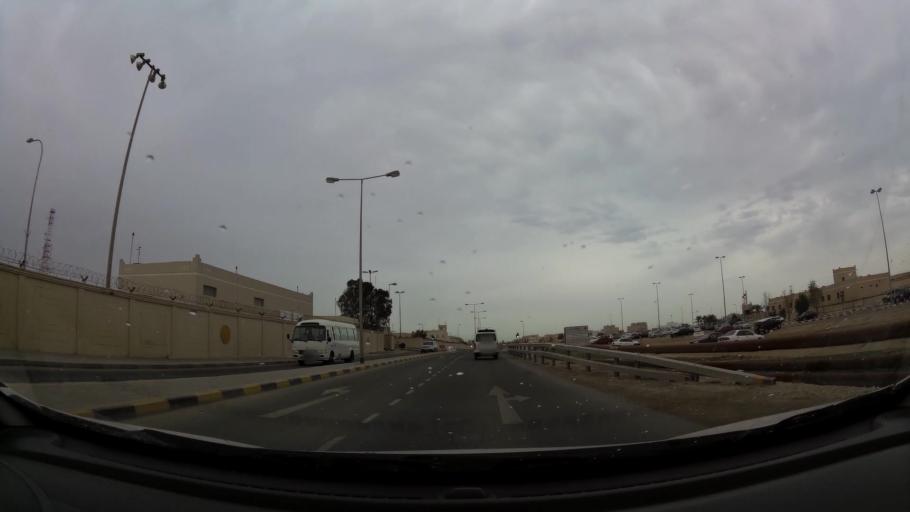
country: BH
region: Central Governorate
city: Madinat Hamad
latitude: 26.1545
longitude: 50.4815
